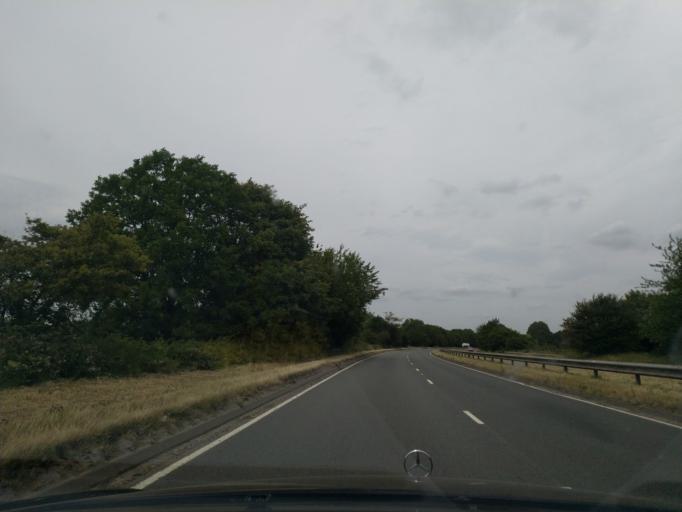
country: GB
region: England
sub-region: Solihull
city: Hampton in Arden
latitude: 52.4232
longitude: -1.6785
